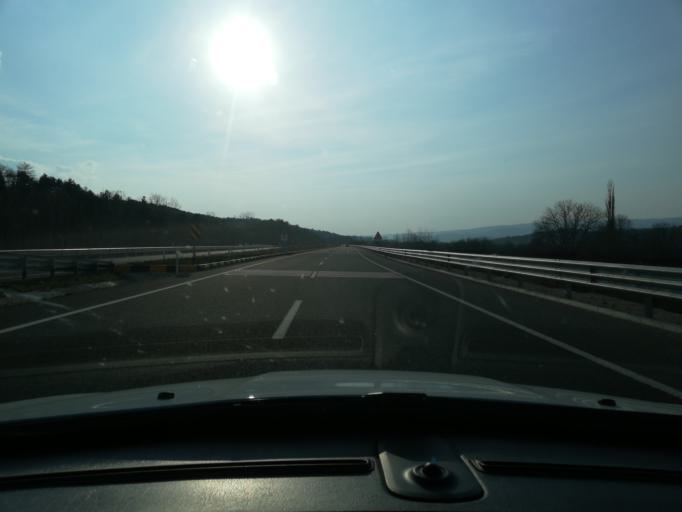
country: TR
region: Kastamonu
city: Igdir
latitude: 41.2274
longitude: 33.1200
